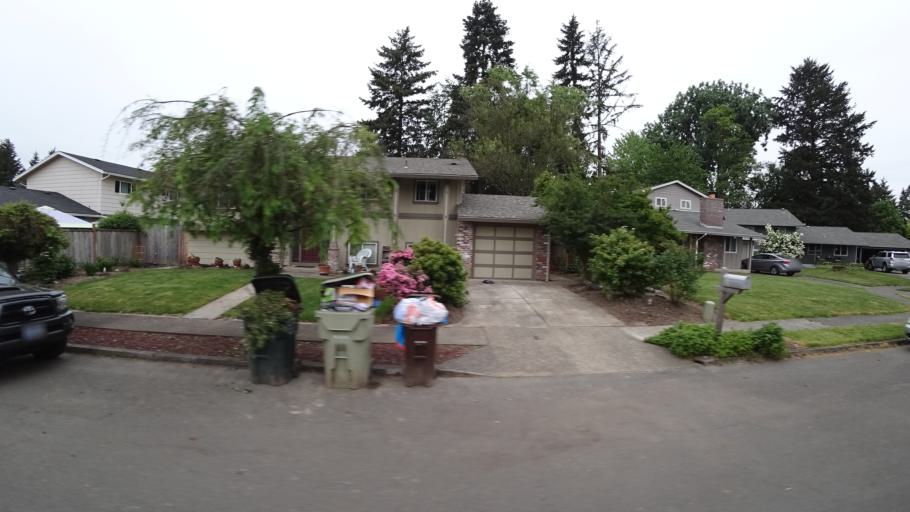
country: US
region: Oregon
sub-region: Washington County
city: Bethany
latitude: 45.5452
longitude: -122.8624
